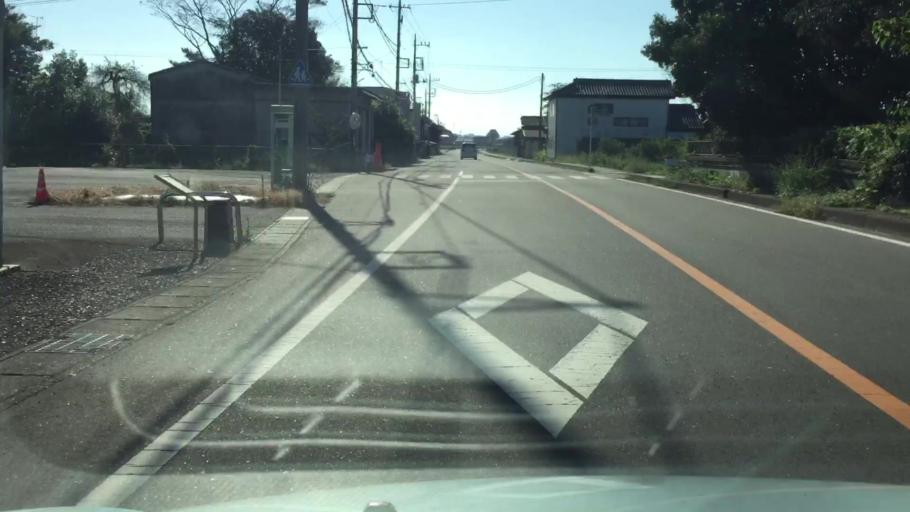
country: JP
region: Tochigi
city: Ujiie
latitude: 36.6839
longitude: 140.0065
